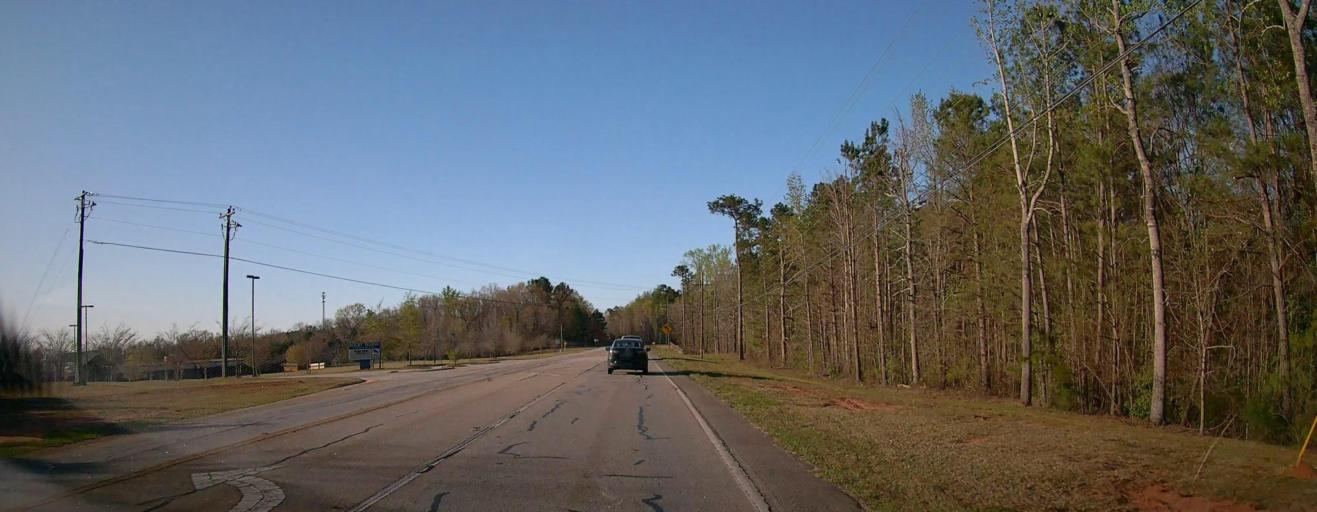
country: US
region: Georgia
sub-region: Newton County
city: Oakwood
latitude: 33.4296
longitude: -83.8957
